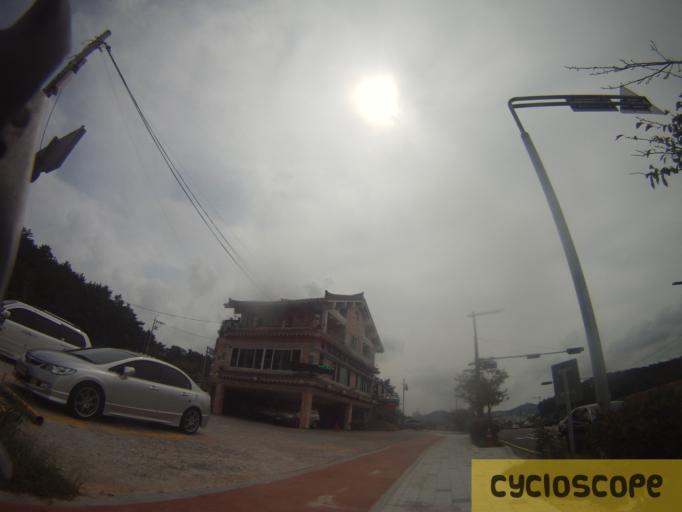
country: KR
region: Busan
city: Kijang
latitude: 35.1924
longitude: 129.2176
